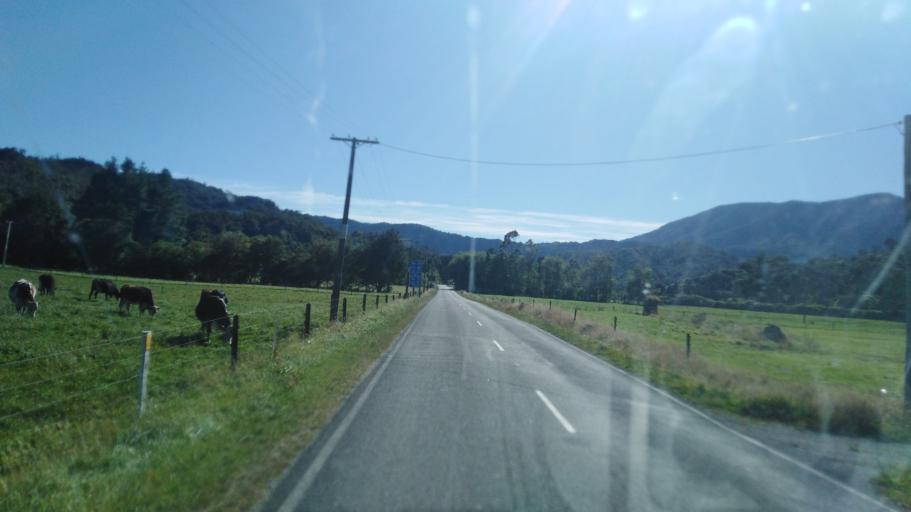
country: NZ
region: West Coast
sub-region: Buller District
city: Westport
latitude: -41.5323
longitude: 171.9625
